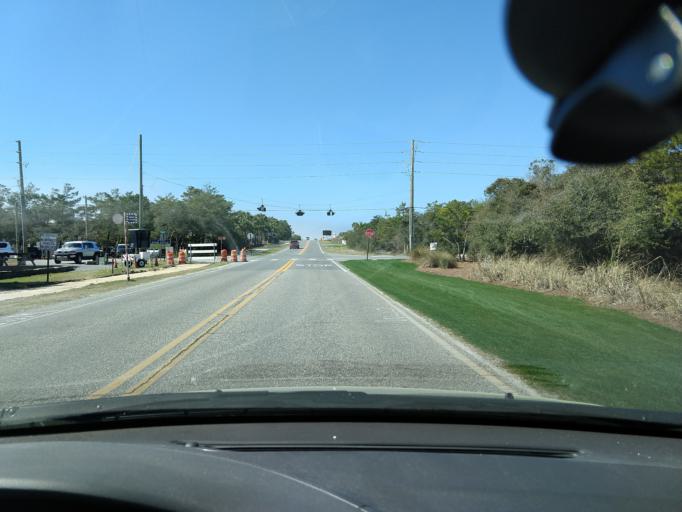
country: US
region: Florida
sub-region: Walton County
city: Seaside
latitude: 30.3405
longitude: -86.2003
